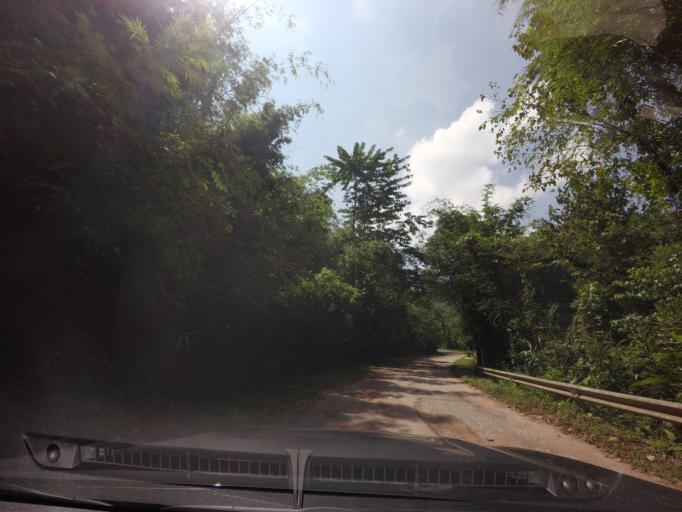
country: TH
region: Loei
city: Na Haeo
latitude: 17.5223
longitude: 100.9375
